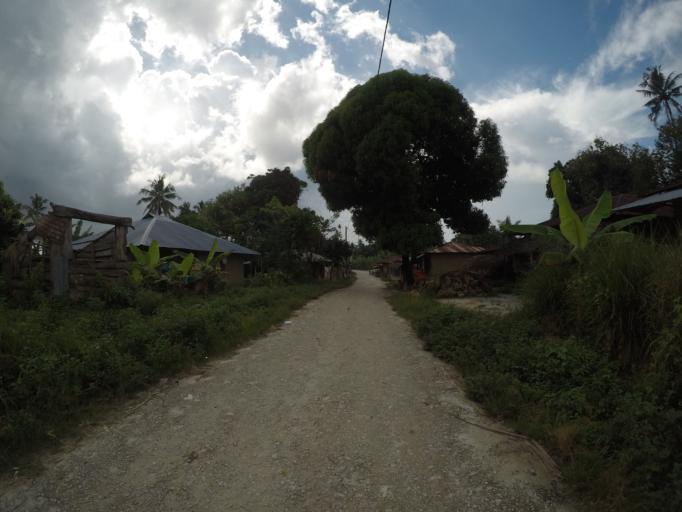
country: TZ
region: Pemba South
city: Mtambile
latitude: -5.3506
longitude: 39.7023
